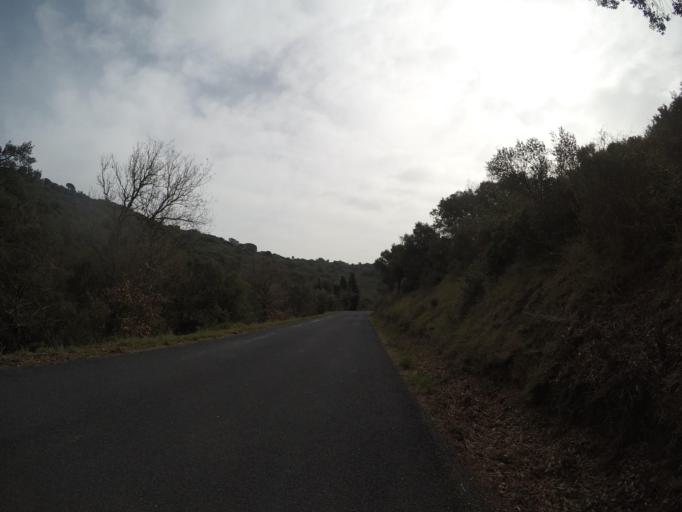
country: FR
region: Languedoc-Roussillon
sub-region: Departement des Pyrenees-Orientales
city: Estagel
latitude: 42.7516
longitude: 2.7202
